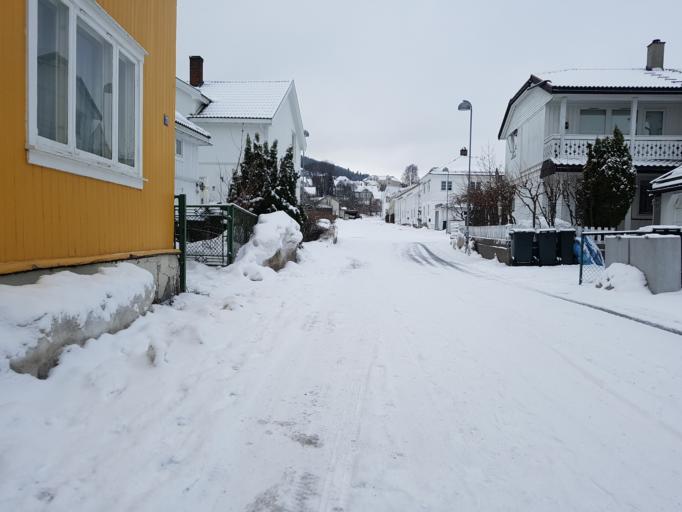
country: NO
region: Buskerud
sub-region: Drammen
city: Drammen
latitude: 59.7375
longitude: 10.1937
